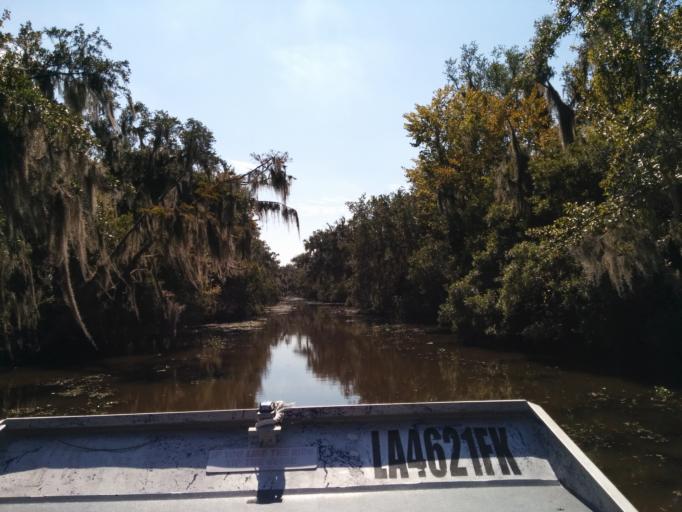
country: US
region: Louisiana
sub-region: Jefferson Parish
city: Barataria
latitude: 29.7188
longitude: -90.1429
